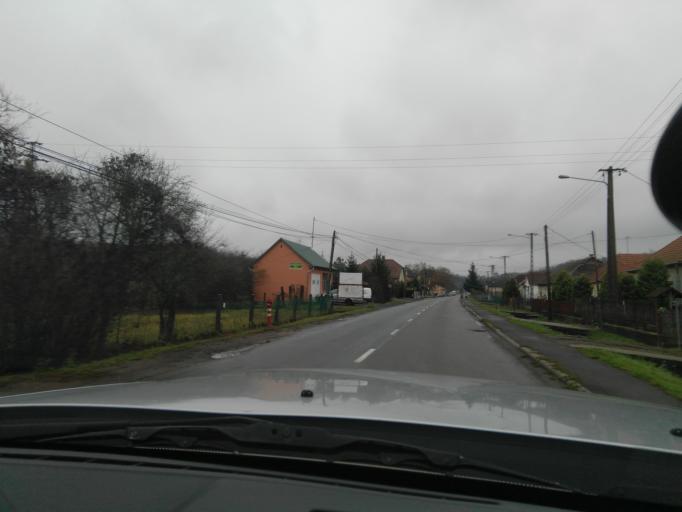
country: HU
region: Nograd
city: Matraterenye
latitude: 48.0279
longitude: 19.9512
